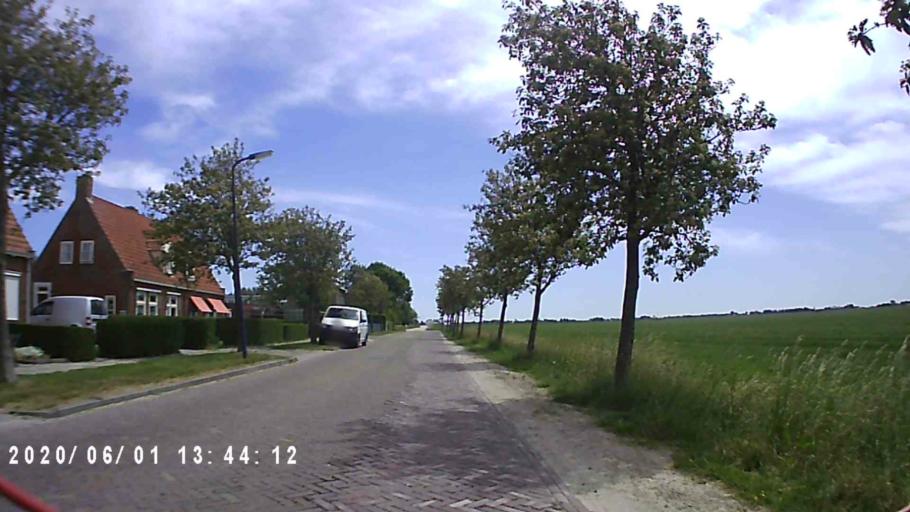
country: NL
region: Friesland
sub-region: Gemeente Littenseradiel
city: Wommels
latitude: 53.0952
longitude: 5.6172
